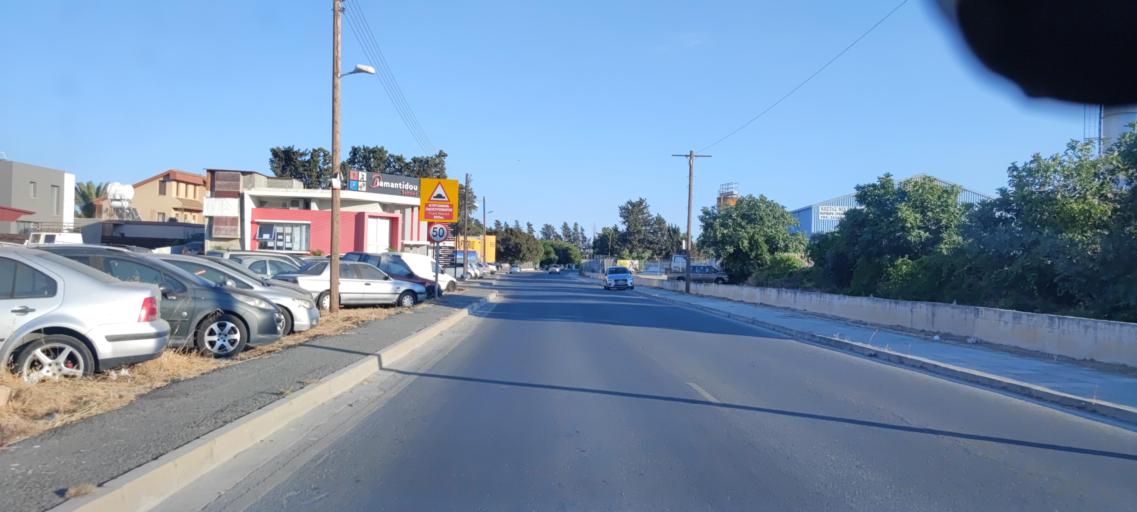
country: CY
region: Limassol
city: Pano Polemidia
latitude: 34.6695
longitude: 32.9980
